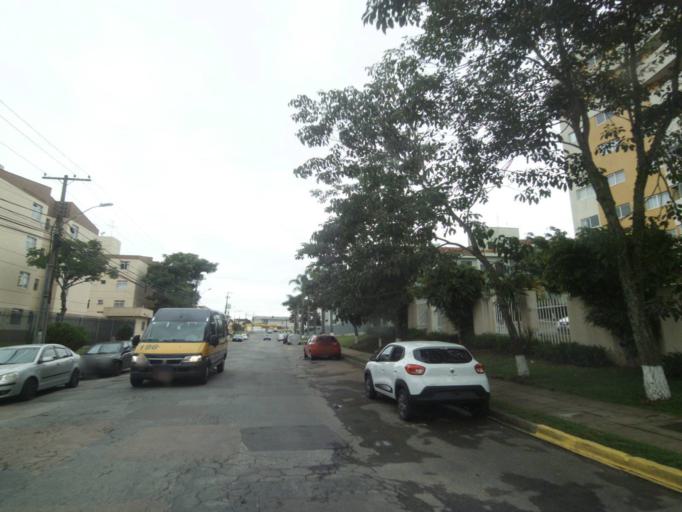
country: BR
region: Parana
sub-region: Curitiba
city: Curitiba
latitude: -25.4596
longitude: -49.3253
